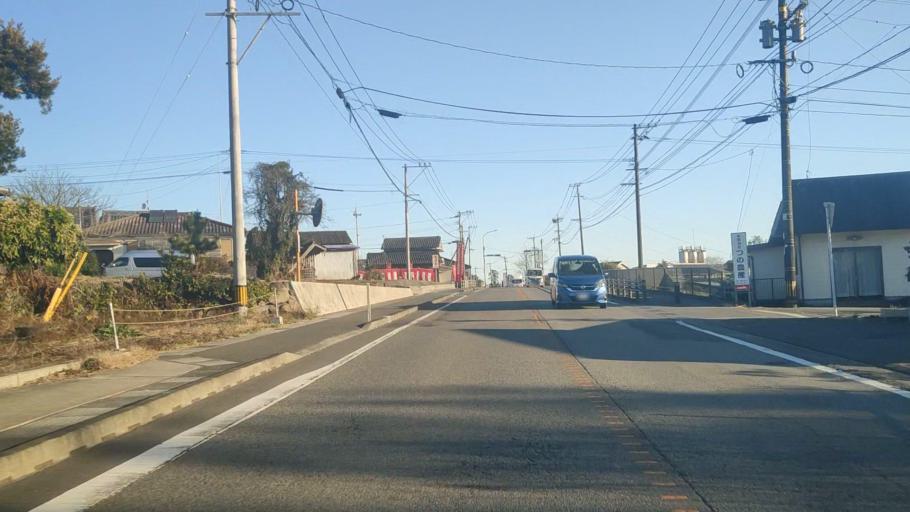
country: JP
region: Miyazaki
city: Takanabe
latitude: 32.2423
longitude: 131.5496
